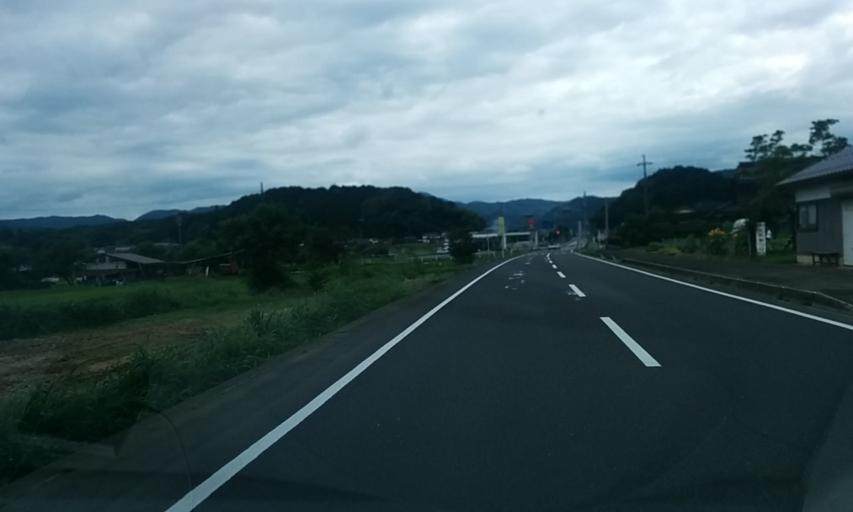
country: JP
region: Kyoto
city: Ayabe
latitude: 35.3217
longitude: 135.2617
